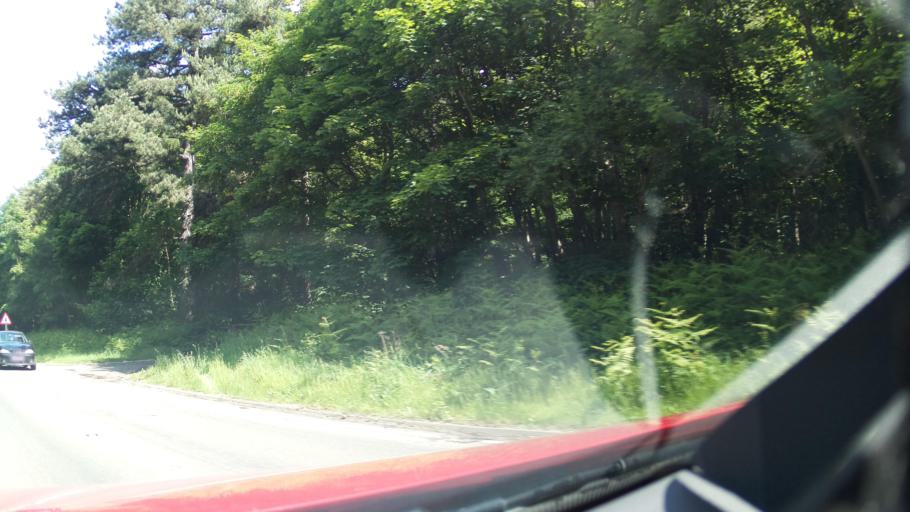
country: GB
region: England
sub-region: North Lincolnshire
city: Broughton
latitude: 53.5506
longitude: -0.5801
